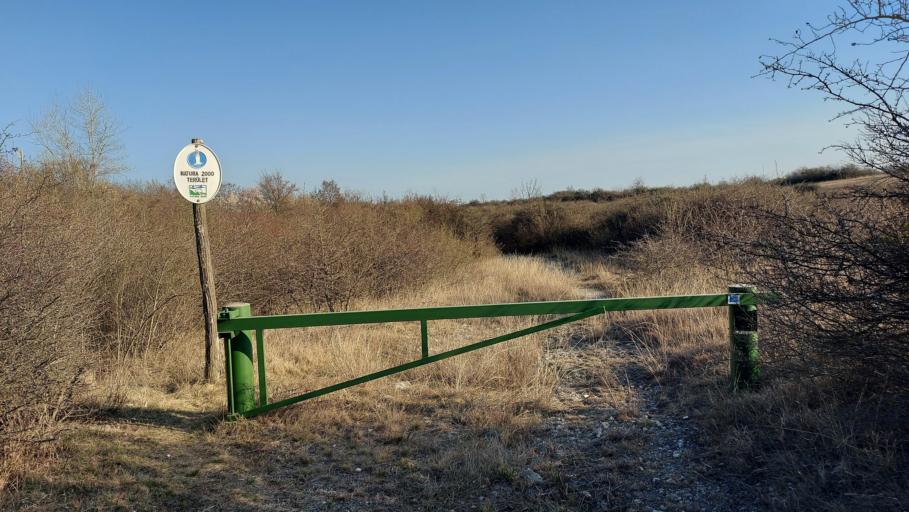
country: HU
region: Pest
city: Diosd
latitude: 47.4286
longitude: 18.9586
